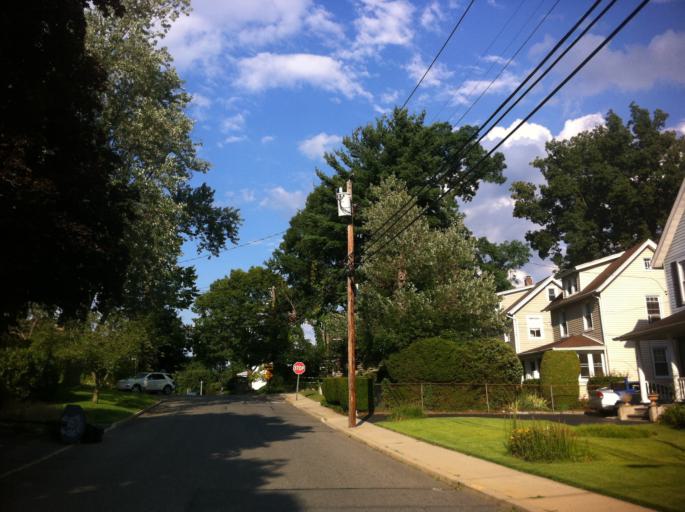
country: US
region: New York
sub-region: Nassau County
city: Glen Head
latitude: 40.8484
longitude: -73.6286
